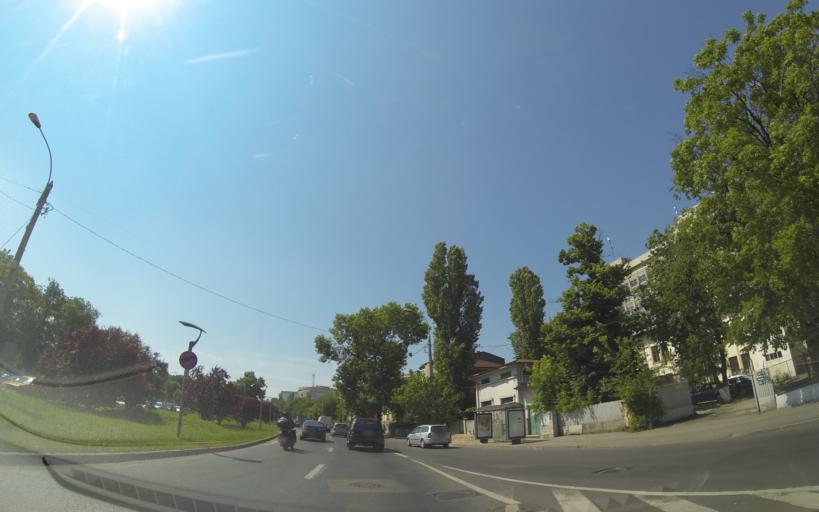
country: RO
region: Bucuresti
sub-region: Municipiul Bucuresti
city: Bucuresti
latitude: 44.4342
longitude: 26.0592
